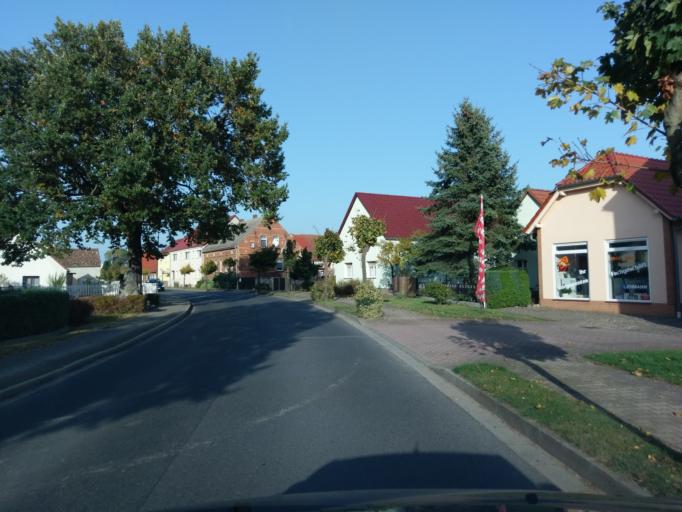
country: DE
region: Brandenburg
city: Falkenberg
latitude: 51.5697
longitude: 13.2507
